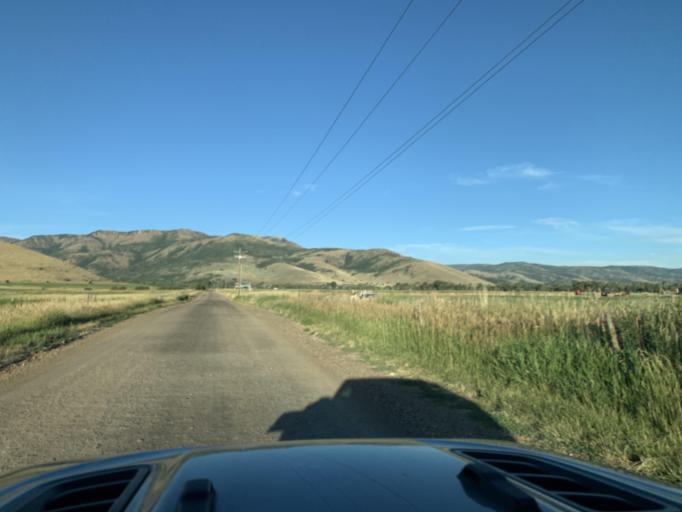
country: US
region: Utah
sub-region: Weber County
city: Wolf Creek
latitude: 41.2931
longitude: -111.7769
